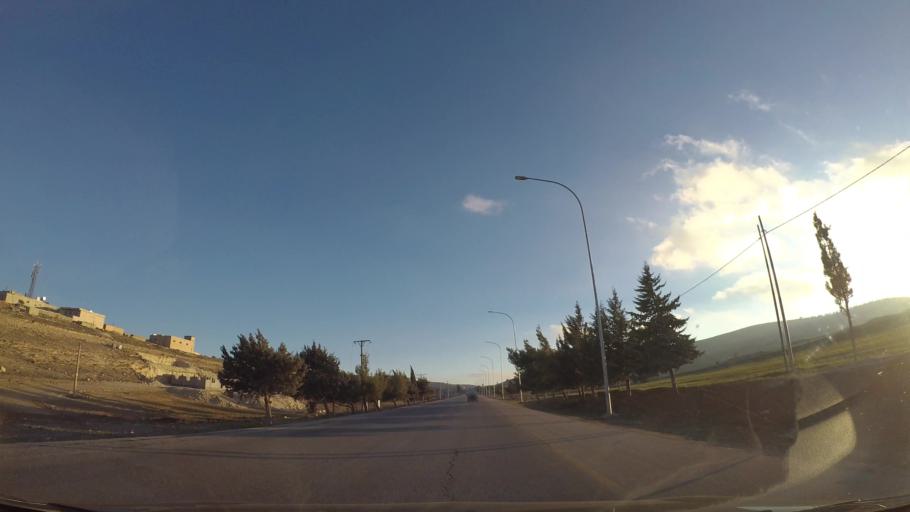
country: JO
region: Ma'an
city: Petra
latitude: 30.4393
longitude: 35.5187
